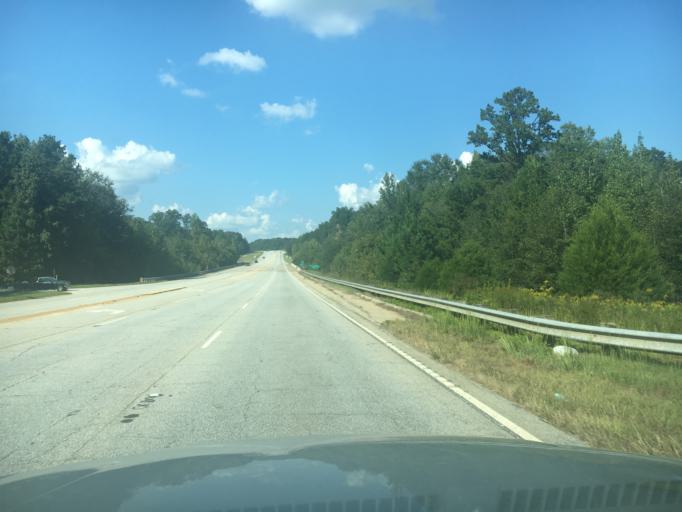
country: US
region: South Carolina
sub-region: Greenwood County
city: Ware Shoals
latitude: 34.3895
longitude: -82.2237
